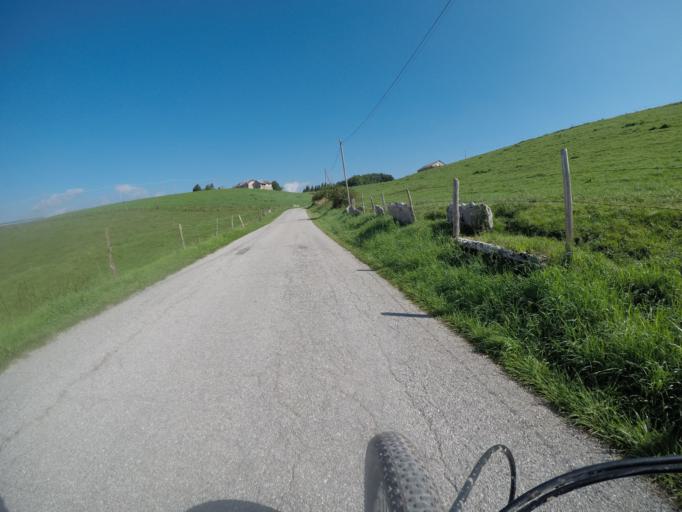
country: IT
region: Veneto
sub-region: Provincia di Vicenza
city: Canove di Roana
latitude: 45.8425
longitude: 11.4998
